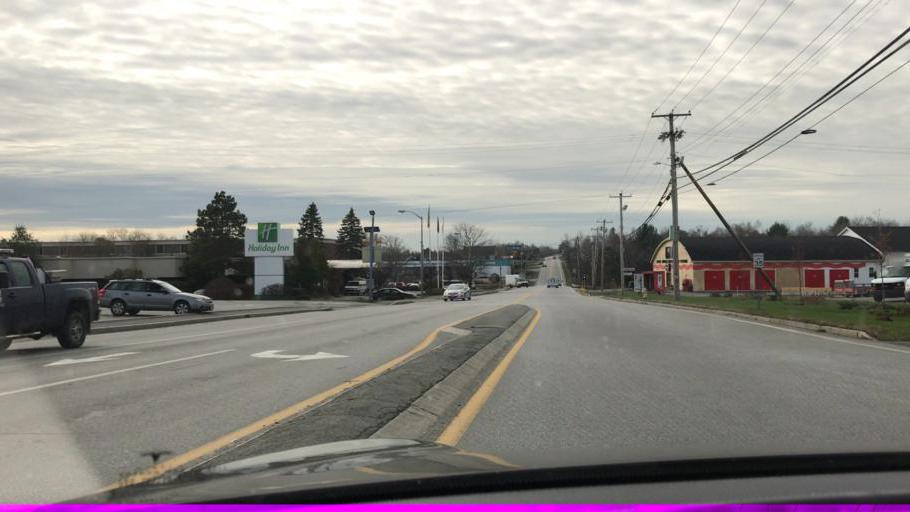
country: US
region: Maine
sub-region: Penobscot County
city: Bangor
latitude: 44.7872
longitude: -68.8128
